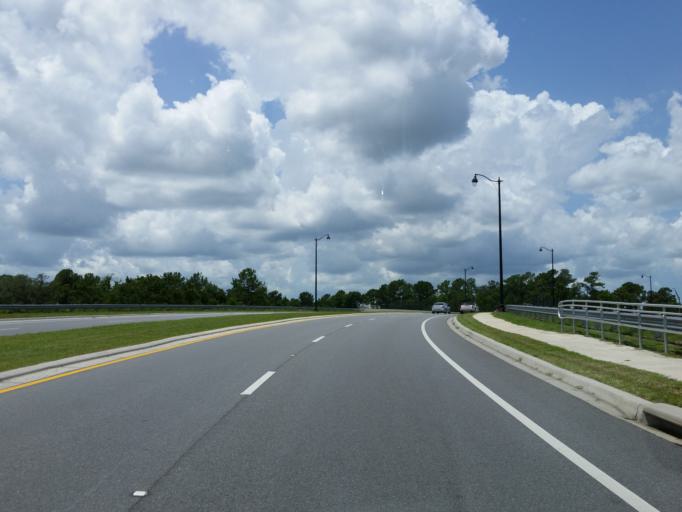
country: US
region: Florida
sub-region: Marion County
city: Ocala
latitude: 29.1435
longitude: -82.1835
